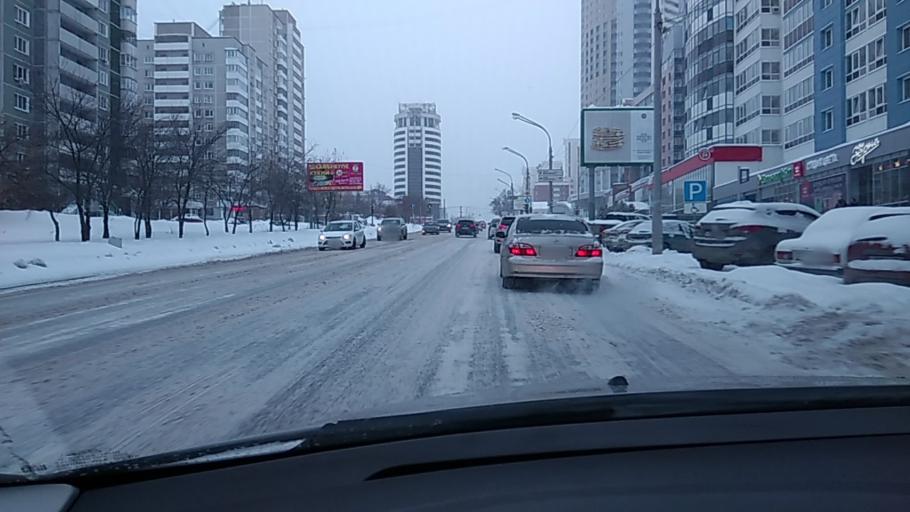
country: RU
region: Sverdlovsk
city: Yekaterinburg
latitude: 56.8259
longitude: 60.5908
